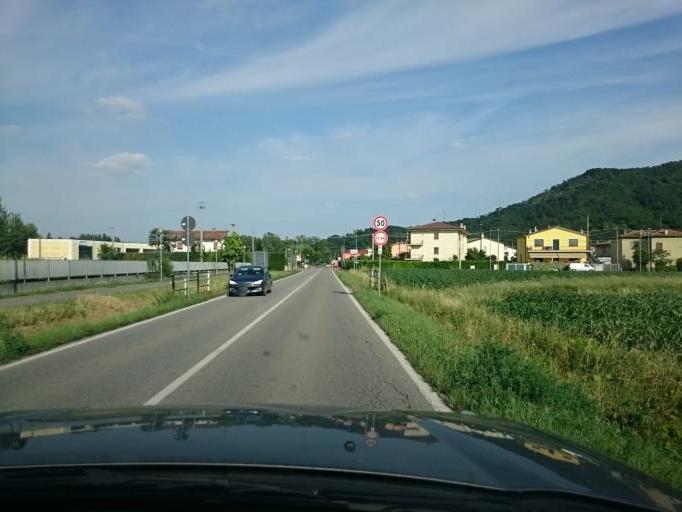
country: IT
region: Veneto
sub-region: Provincia di Padova
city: Torreglia
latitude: 45.3328
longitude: 11.7570
